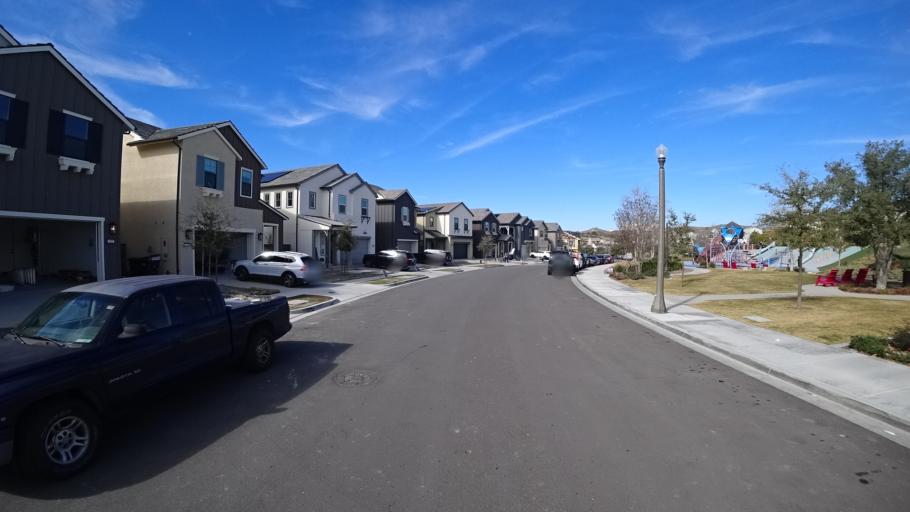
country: US
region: California
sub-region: Orange County
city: Ladera Ranch
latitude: 33.5510
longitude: -117.6009
